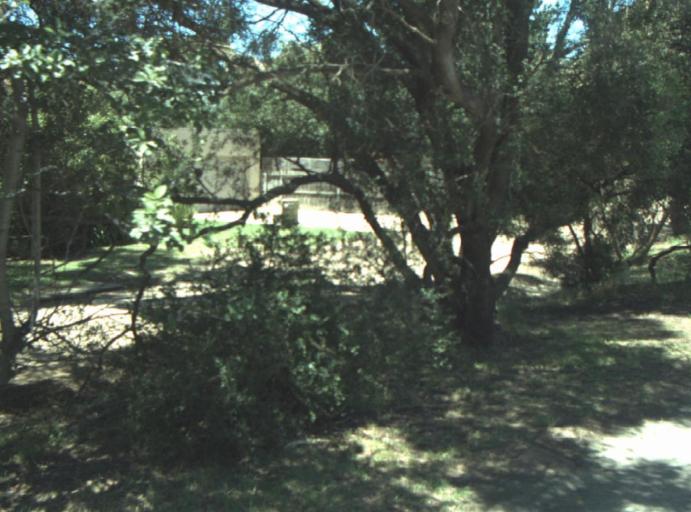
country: AU
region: Victoria
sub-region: Greater Geelong
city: Leopold
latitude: -38.2554
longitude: 144.5360
